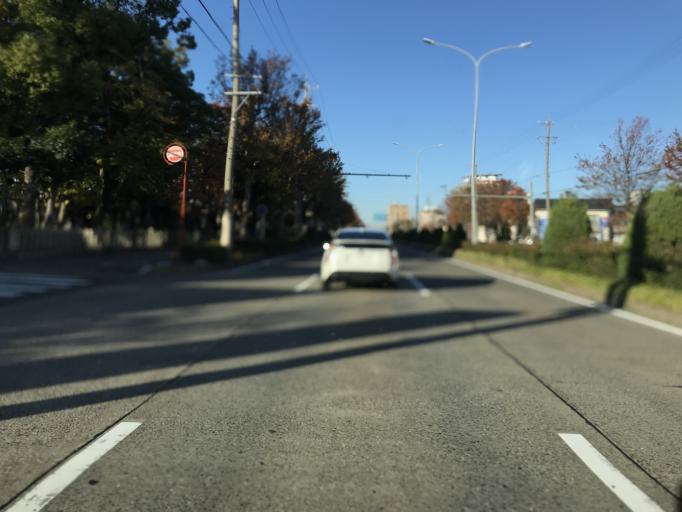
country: JP
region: Aichi
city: Nagoya-shi
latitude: 35.1470
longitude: 136.8721
